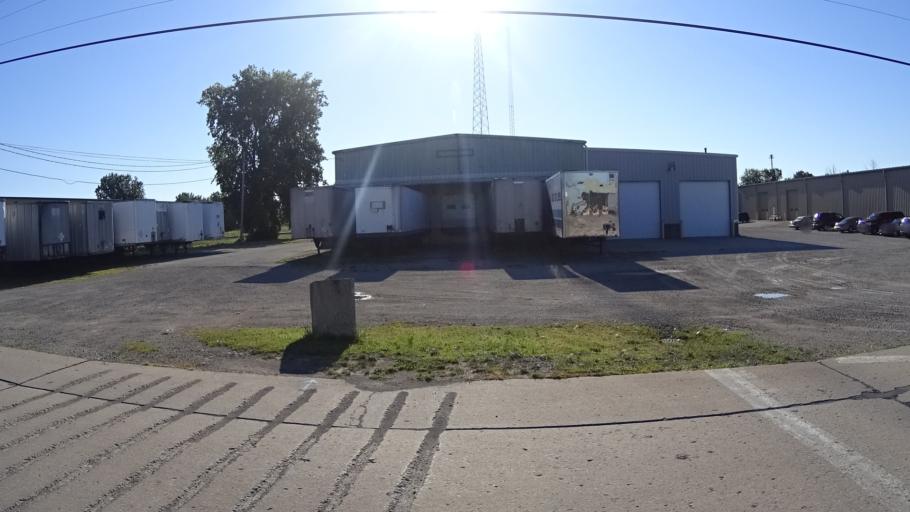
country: US
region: Ohio
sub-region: Erie County
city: Sandusky
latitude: 41.4363
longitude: -82.7433
